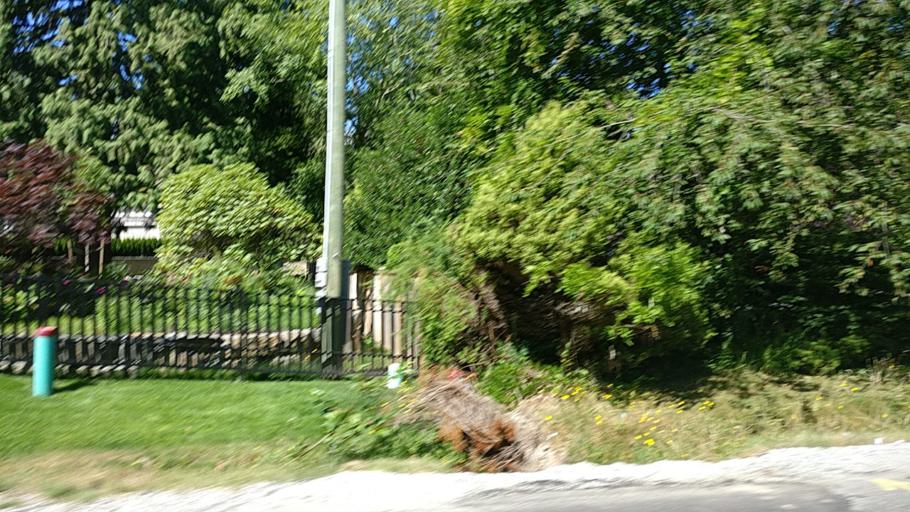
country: CA
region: British Columbia
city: Surrey
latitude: 49.0557
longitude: -122.8564
